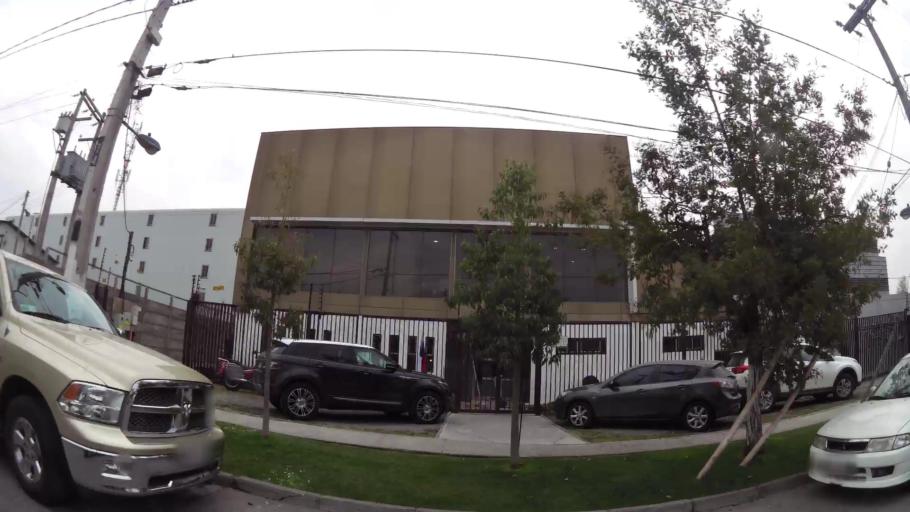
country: CL
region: Santiago Metropolitan
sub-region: Provincia de Santiago
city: Villa Presidente Frei, Nunoa, Santiago, Chile
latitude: -33.4934
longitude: -70.6078
